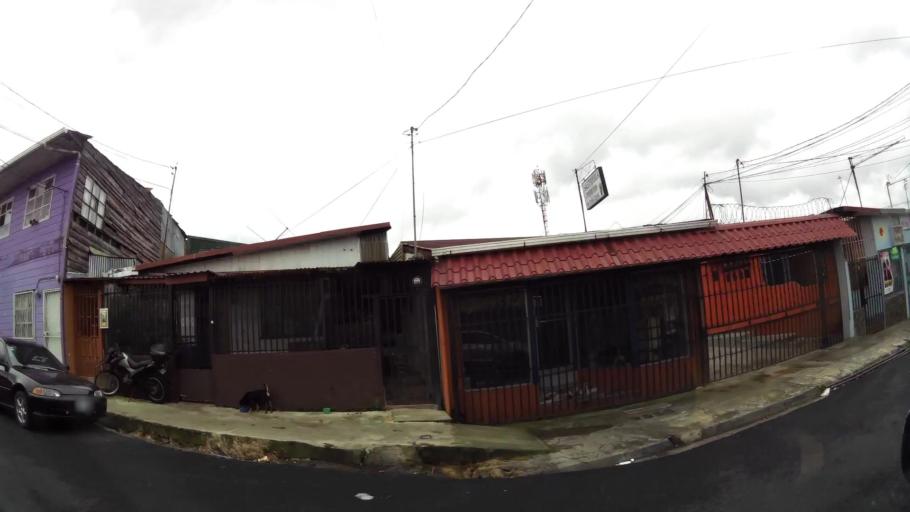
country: CR
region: San Jose
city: Calle Blancos
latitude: 9.9487
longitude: -84.0662
